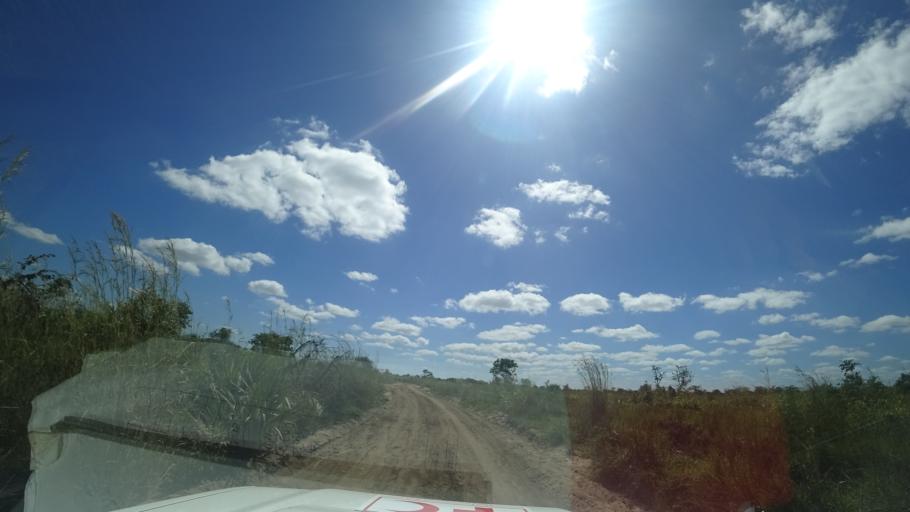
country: MZ
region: Sofala
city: Dondo
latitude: -19.4662
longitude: 34.5966
